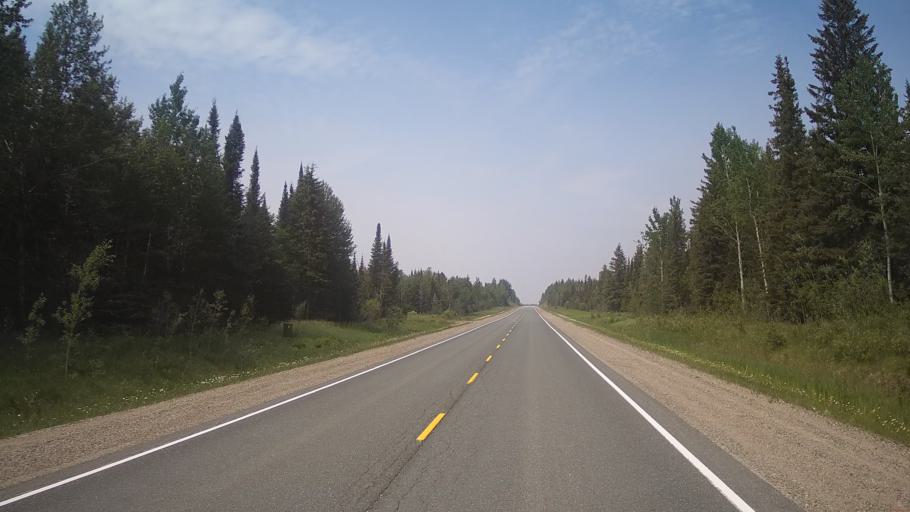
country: CA
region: Ontario
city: Timmins
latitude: 48.7425
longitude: -81.3566
